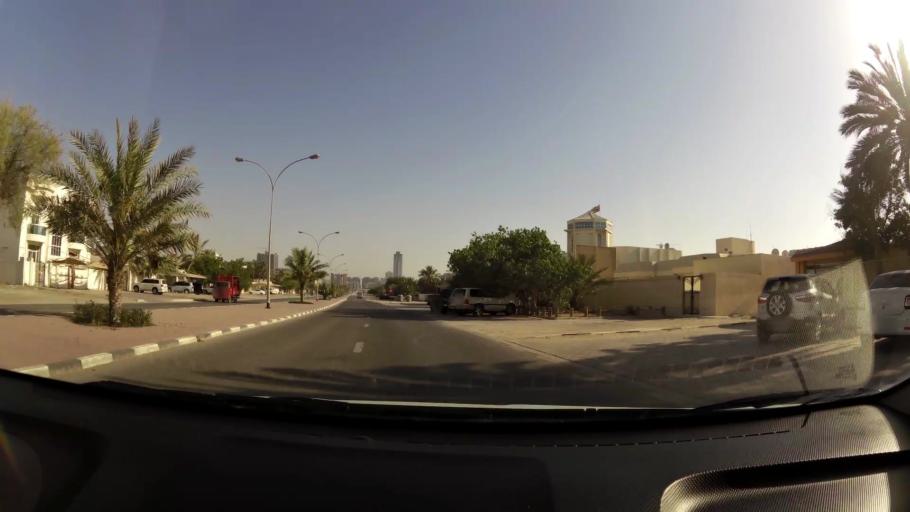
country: AE
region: Ajman
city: Ajman
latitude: 25.4040
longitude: 55.4632
